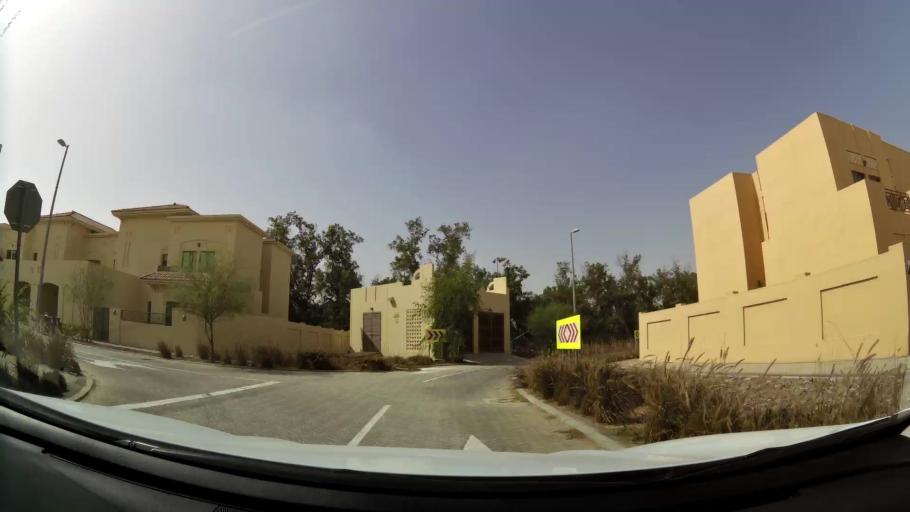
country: AE
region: Abu Dhabi
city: Abu Dhabi
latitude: 24.4102
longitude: 54.5332
